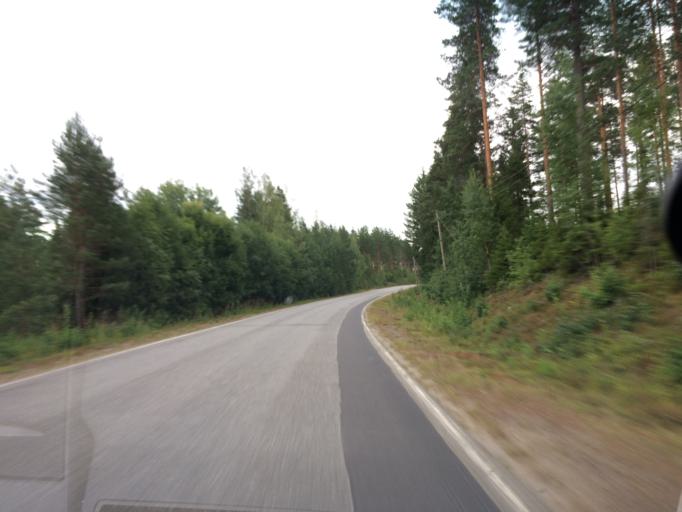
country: FI
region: Haeme
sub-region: Haemeenlinna
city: Tuulos
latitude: 61.2225
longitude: 24.7214
